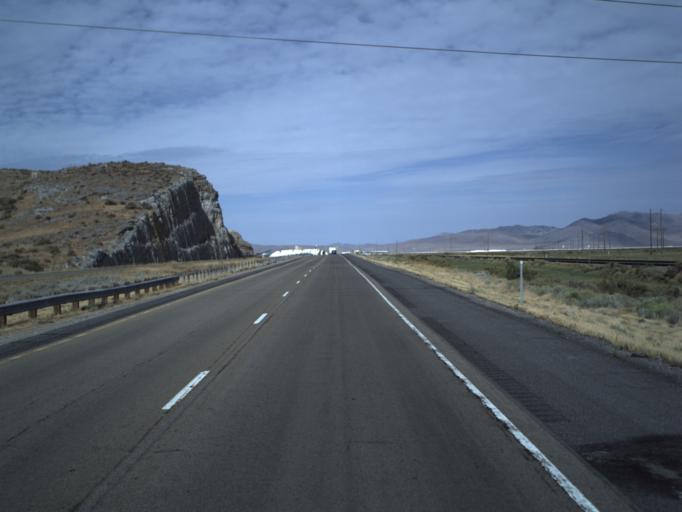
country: US
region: Utah
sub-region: Tooele County
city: Grantsville
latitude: 40.7429
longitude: -112.6310
